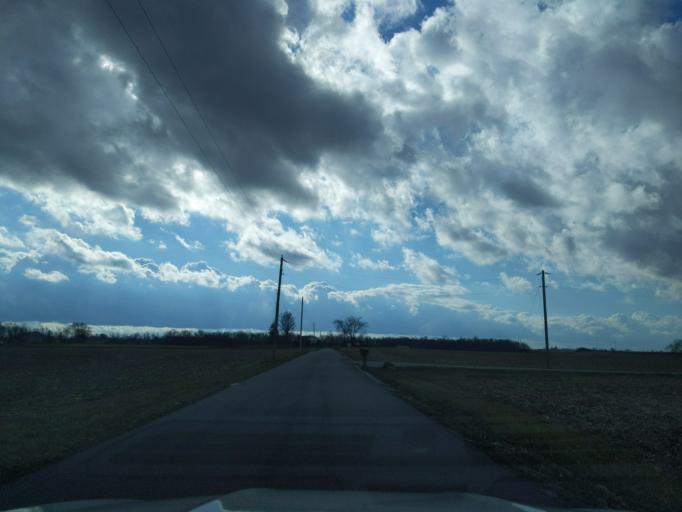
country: US
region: Indiana
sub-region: Decatur County
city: Greensburg
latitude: 39.3757
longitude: -85.5034
